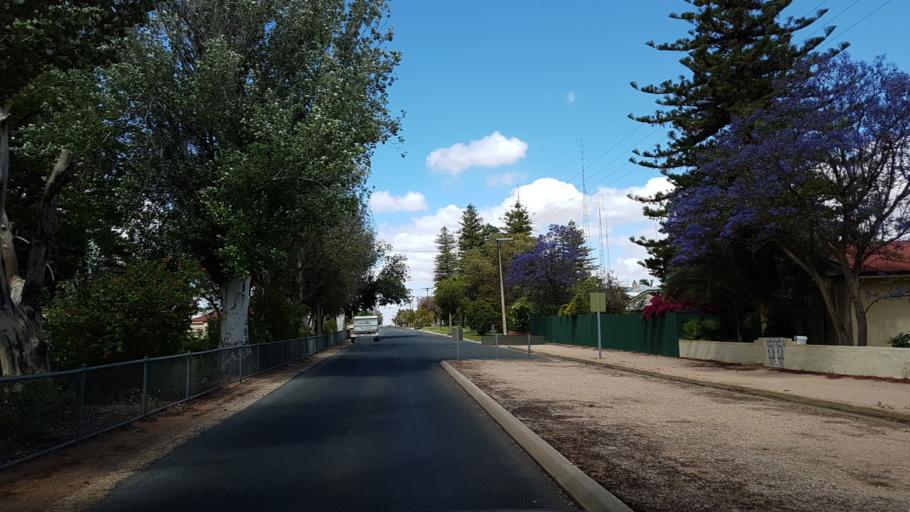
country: AU
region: South Australia
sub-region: Loxton Waikerie
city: Waikerie
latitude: -34.1825
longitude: 139.9813
